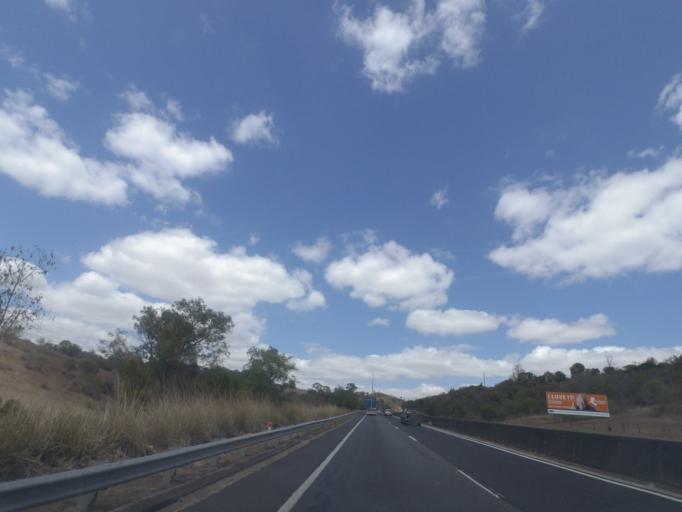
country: AU
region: Queensland
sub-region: Ipswich
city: Thagoona
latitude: -27.5650
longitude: 152.5710
